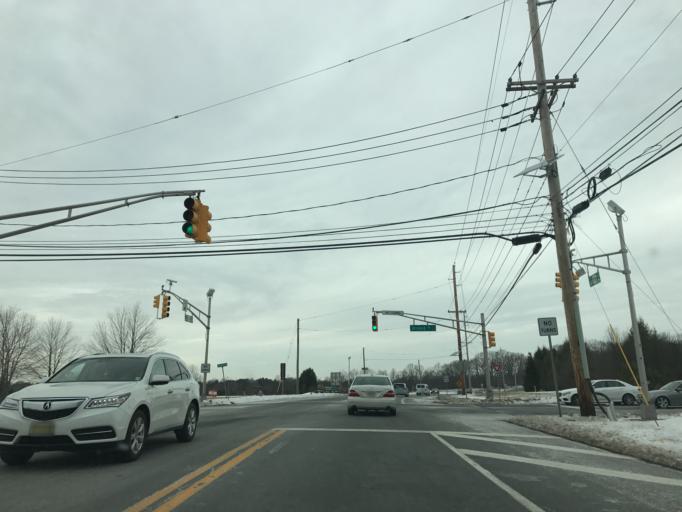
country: US
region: New Jersey
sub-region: Somerset County
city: Ten Mile Run
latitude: 40.4167
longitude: -74.6523
